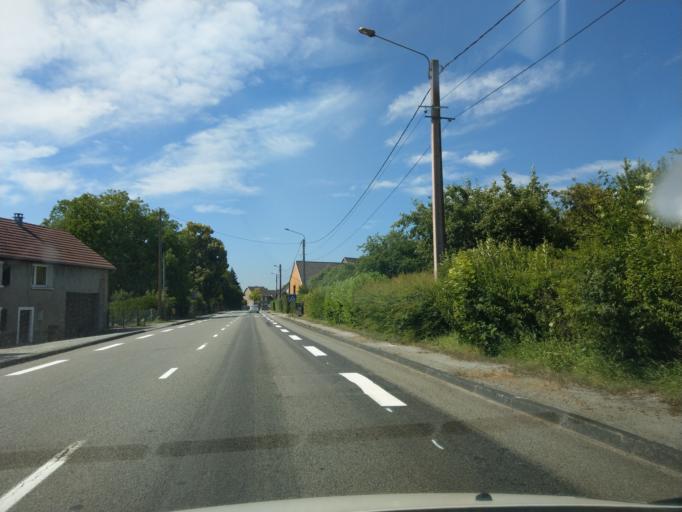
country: FR
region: Franche-Comte
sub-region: Territoire de Belfort
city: Chevremont
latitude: 47.6725
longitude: 6.9242
